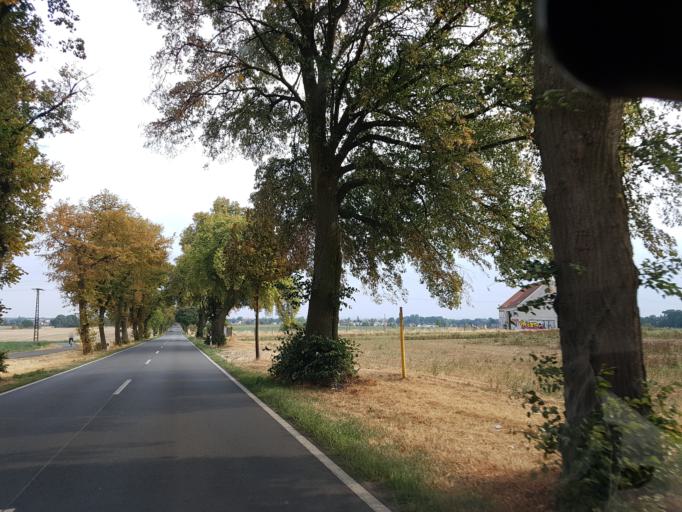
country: DE
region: Saxony-Anhalt
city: Wittenburg
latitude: 51.8898
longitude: 12.6240
